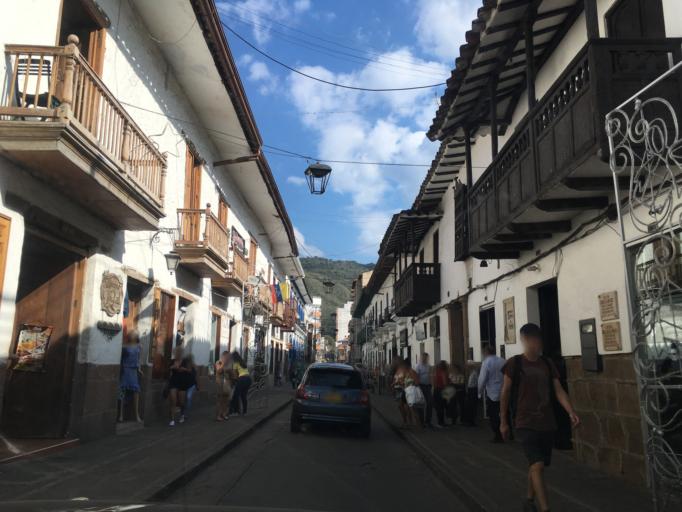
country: CO
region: Santander
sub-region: San Gil
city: San Gil
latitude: 6.5549
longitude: -73.1328
